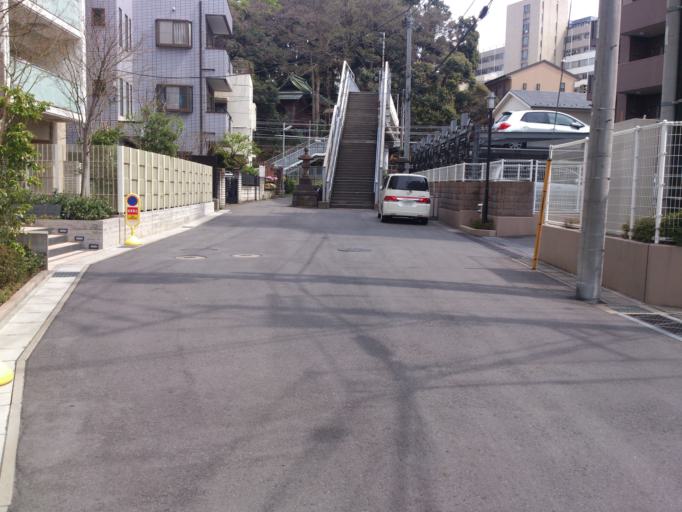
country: JP
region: Chiba
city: Matsudo
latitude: 35.7893
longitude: 139.9018
